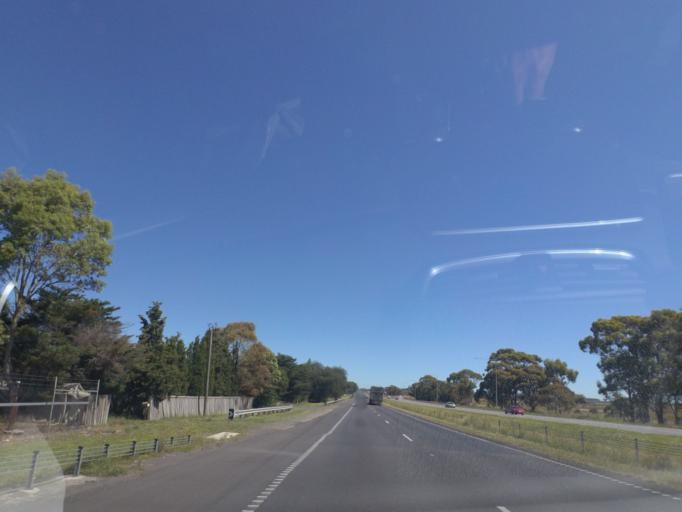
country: AU
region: Victoria
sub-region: Hume
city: Craigieburn
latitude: -37.5317
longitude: 144.9471
